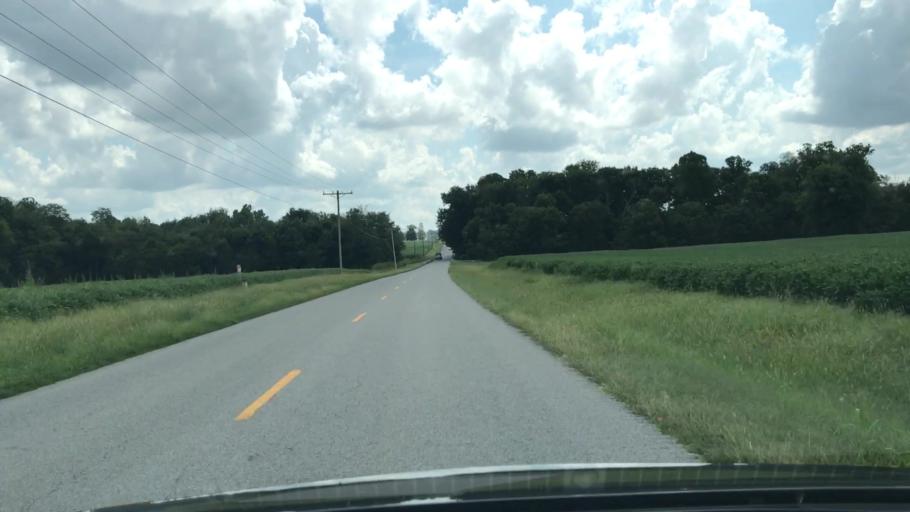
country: US
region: Kentucky
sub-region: Todd County
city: Elkton
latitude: 36.7238
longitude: -87.0843
